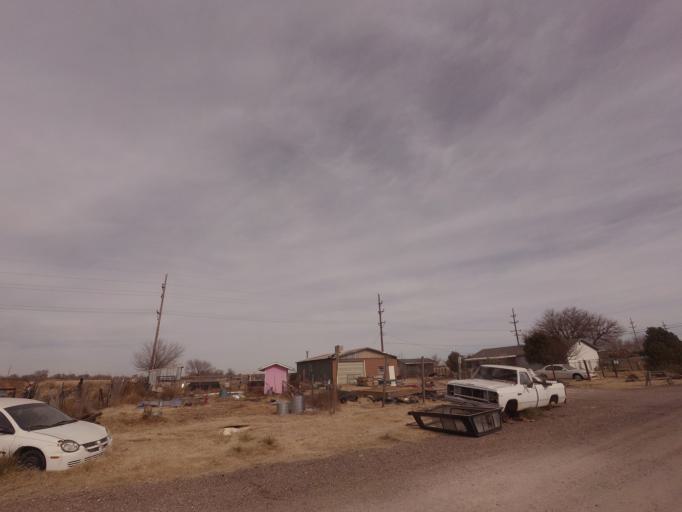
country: US
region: New Mexico
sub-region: Curry County
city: Clovis
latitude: 34.4115
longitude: -103.2455
